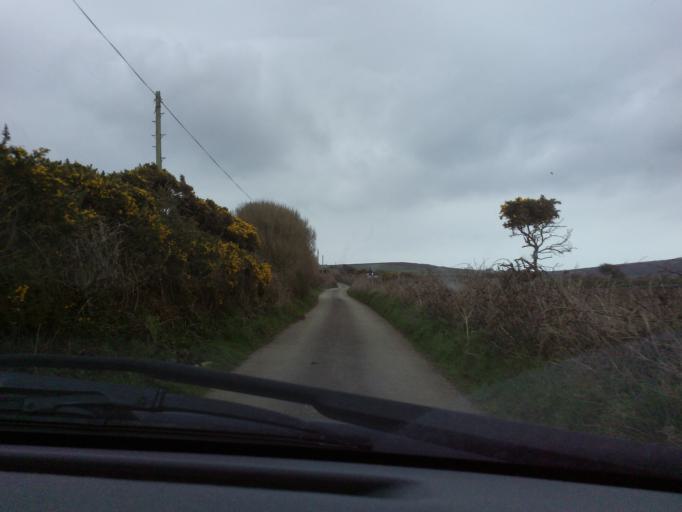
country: GB
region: England
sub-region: Cornwall
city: Saint Just
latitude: 50.1068
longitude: -5.6685
